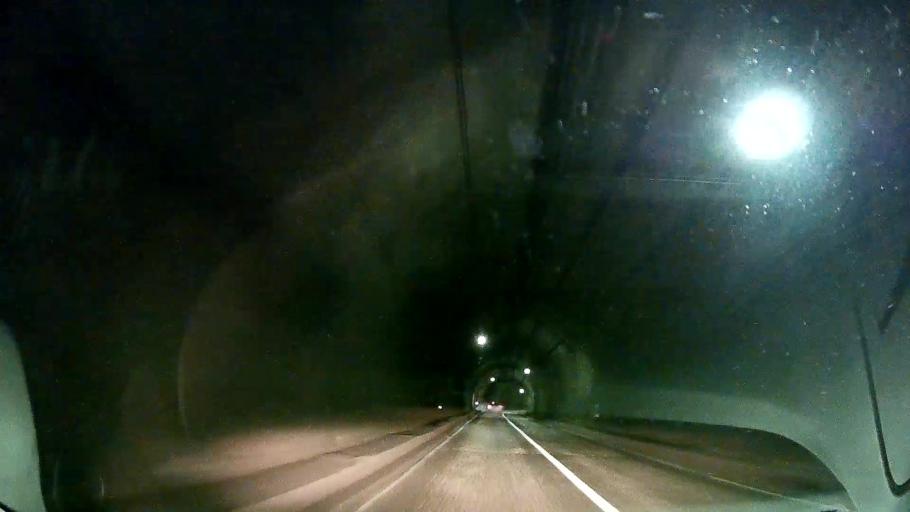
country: JP
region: Nagano
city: Toyoshina
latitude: 36.1787
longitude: 137.6334
